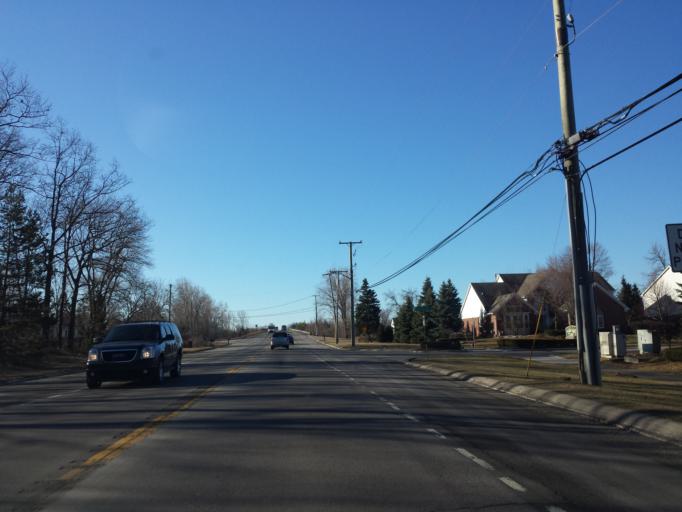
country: US
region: Michigan
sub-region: Oakland County
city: Rochester Hills
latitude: 42.6449
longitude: -83.1525
